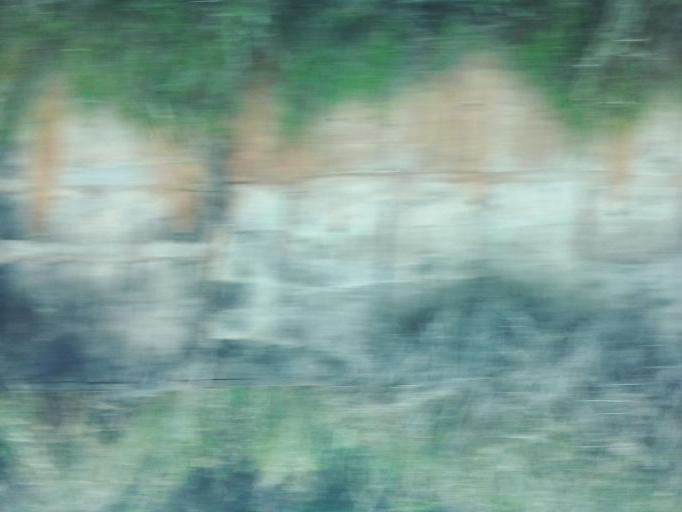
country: BR
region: Minas Gerais
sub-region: Joao Monlevade
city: Joao Monlevade
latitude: -19.8574
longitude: -43.1205
